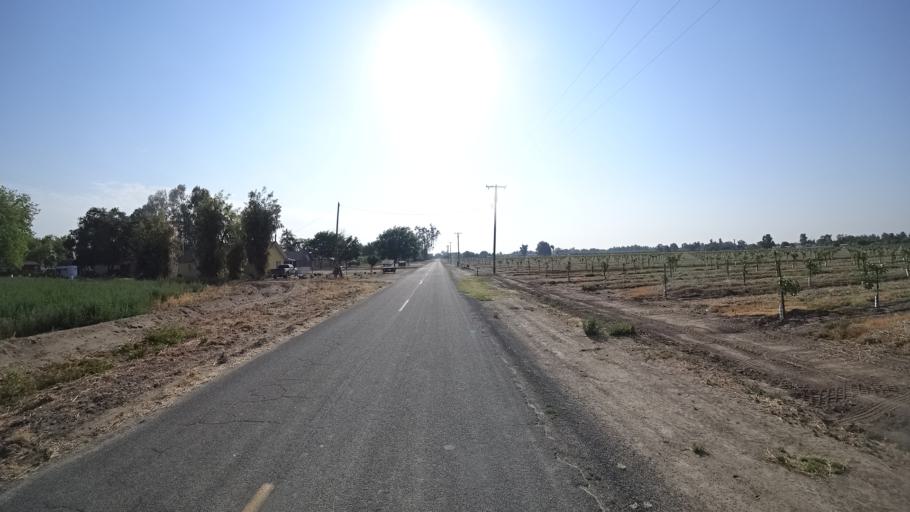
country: US
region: California
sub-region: Fresno County
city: Riverdale
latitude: 36.3585
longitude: -119.8412
